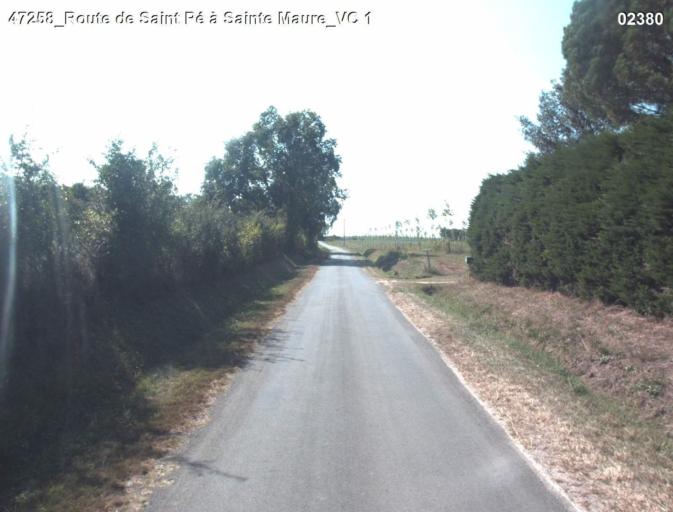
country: FR
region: Midi-Pyrenees
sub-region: Departement du Gers
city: Montreal
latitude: 44.0127
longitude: 0.1485
